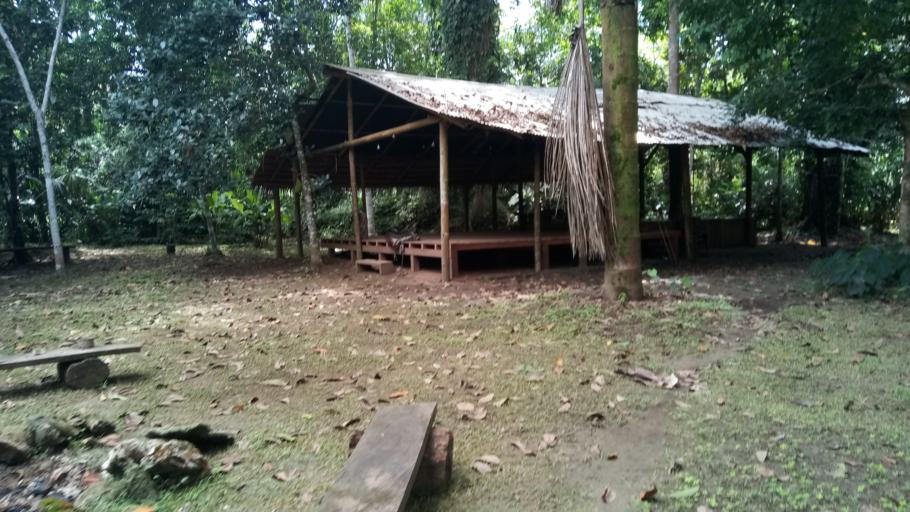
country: CR
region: Limon
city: Sixaola
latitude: 9.6226
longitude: -82.6212
